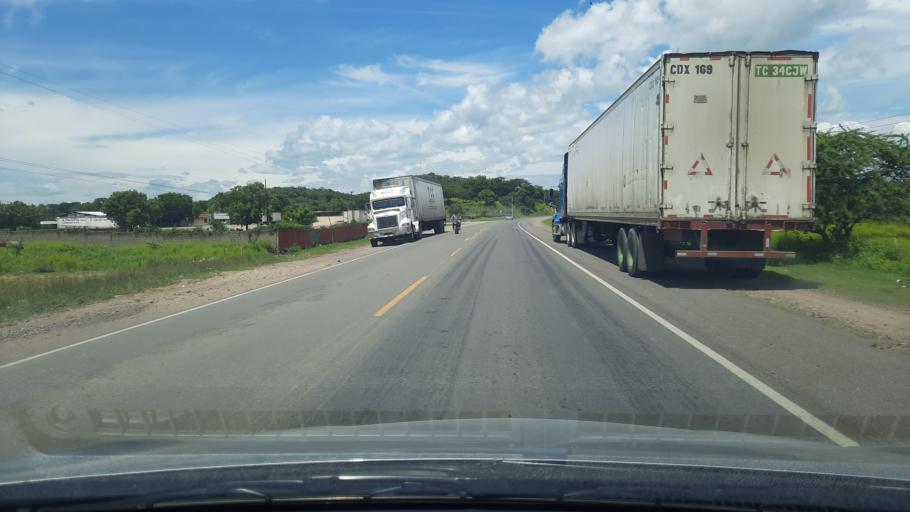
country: NI
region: Chinandega
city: Somotillo
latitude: 13.0546
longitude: -86.9155
